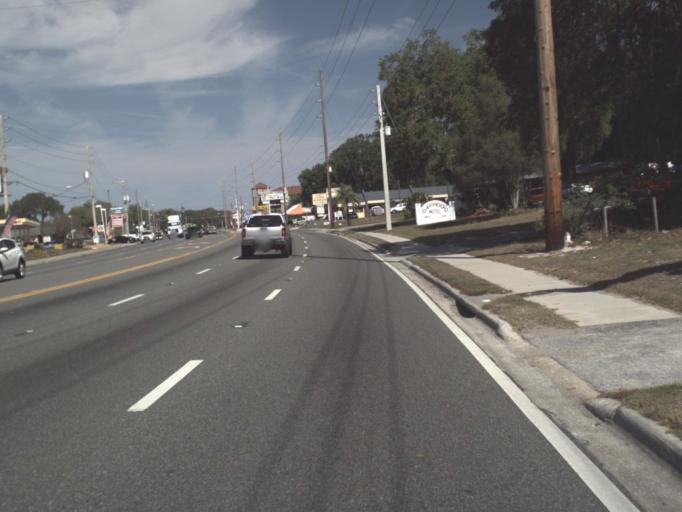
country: US
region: Florida
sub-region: Lake County
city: Fruitland Park
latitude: 28.8400
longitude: -81.8933
